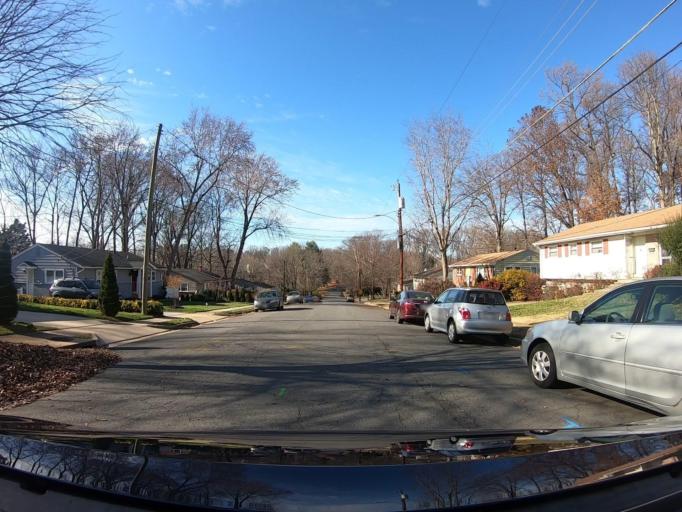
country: US
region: Virginia
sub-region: Fairfax County
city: Merrifield
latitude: 38.8809
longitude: -77.2484
